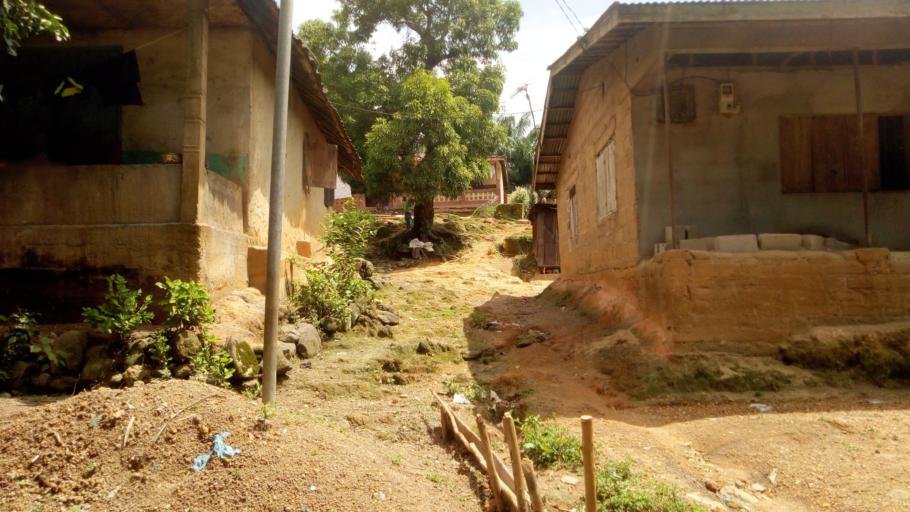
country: SL
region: Northern Province
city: Magburaka
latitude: 8.7240
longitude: -11.9511
